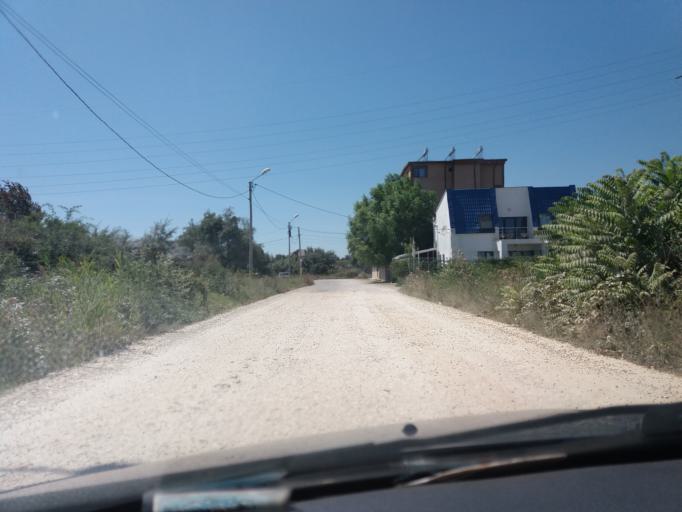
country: RO
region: Constanta
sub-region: Comuna Navodari
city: Navodari
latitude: 44.3215
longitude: 28.6298
